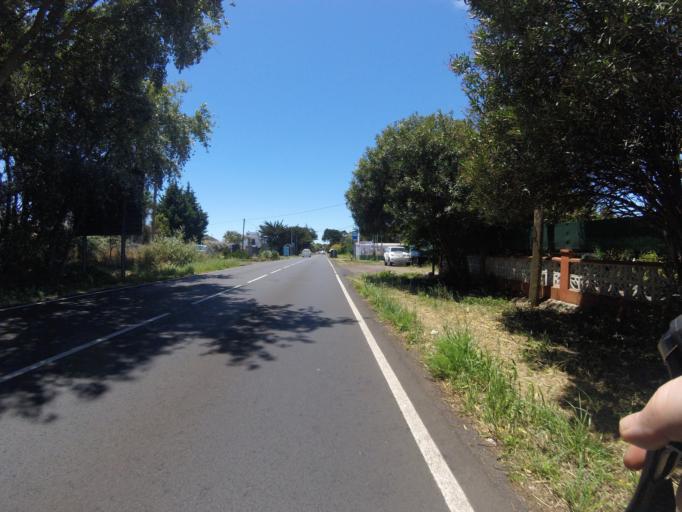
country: ES
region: Canary Islands
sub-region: Provincia de Santa Cruz de Tenerife
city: Tegueste
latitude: 28.5032
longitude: -16.3124
